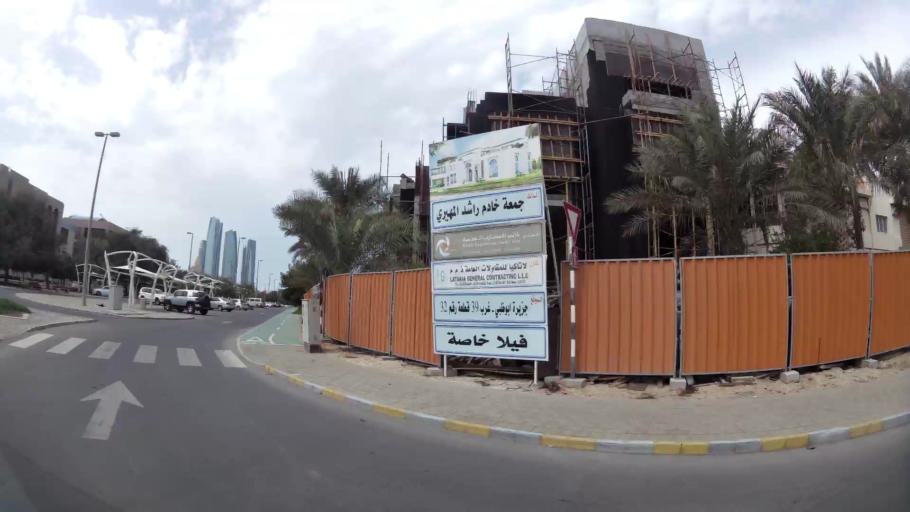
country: AE
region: Abu Dhabi
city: Abu Dhabi
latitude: 24.4575
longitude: 54.3386
